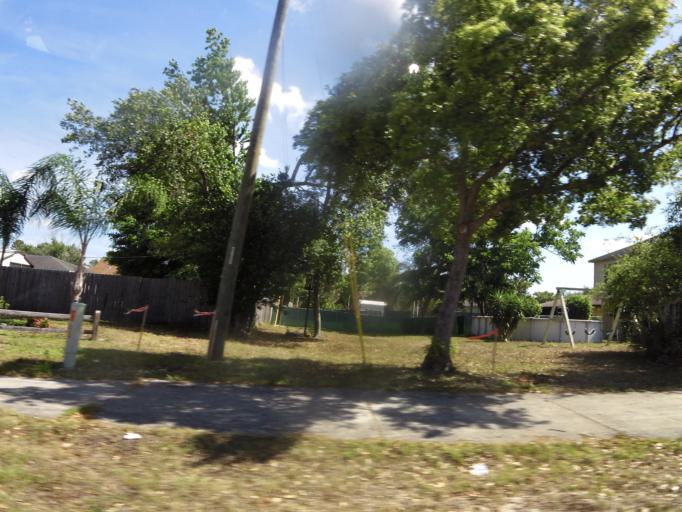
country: US
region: Florida
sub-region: Volusia County
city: Lake Helen
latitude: 28.9398
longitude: -81.2195
